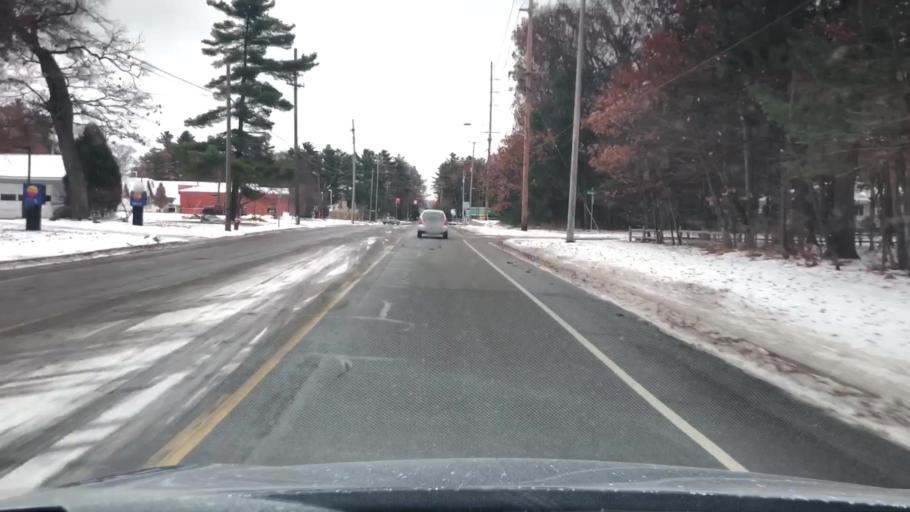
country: US
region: Michigan
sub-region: Grand Traverse County
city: Traverse City
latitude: 44.7586
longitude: -85.5815
